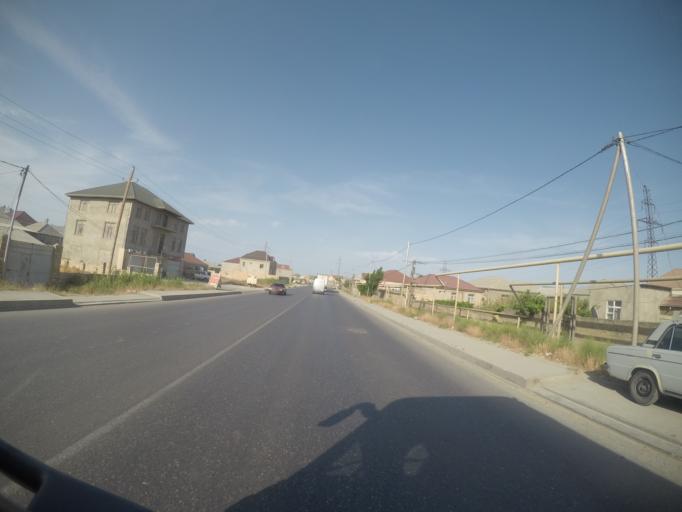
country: AZ
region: Baki
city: Bilajari
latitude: 40.4480
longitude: 49.8010
